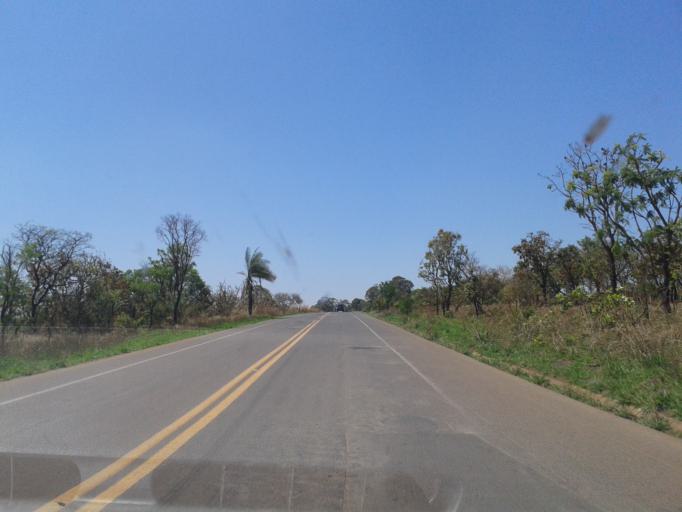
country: BR
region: Minas Gerais
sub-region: Araxa
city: Araxa
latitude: -19.3841
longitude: -47.3450
